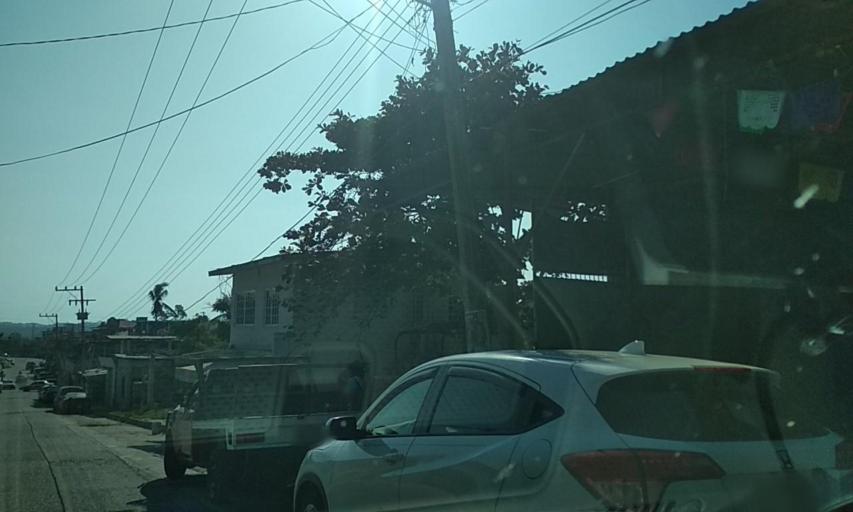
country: MX
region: Veracruz
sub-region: Papantla
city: El Chote
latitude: 20.4047
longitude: -97.3385
